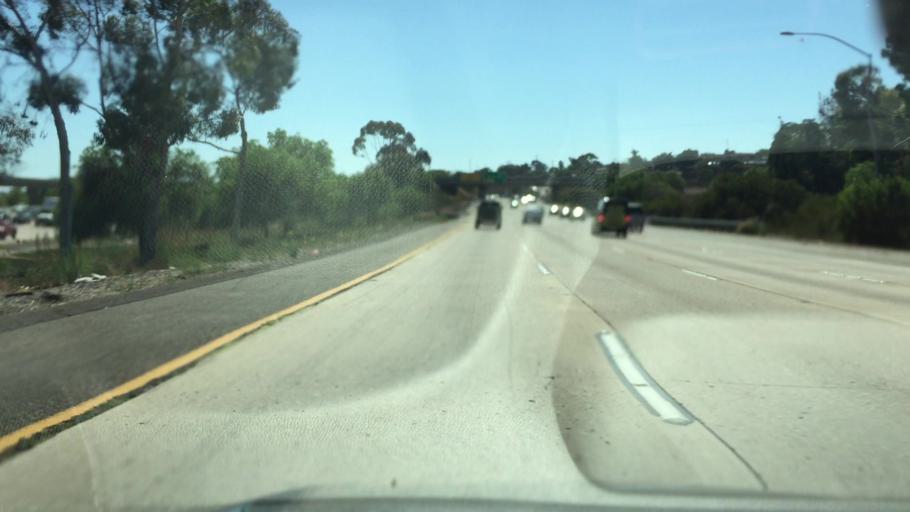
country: US
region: California
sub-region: San Diego County
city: National City
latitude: 32.7179
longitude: -117.1135
